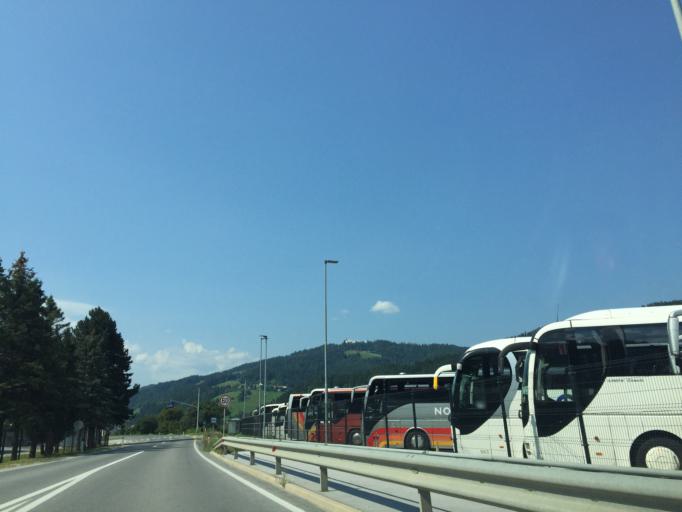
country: SI
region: Slovenj Gradec
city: Pamece
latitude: 46.5273
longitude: 15.0794
